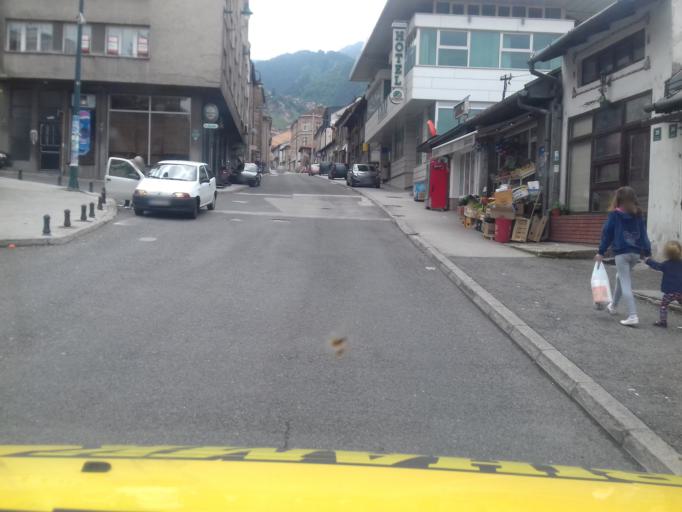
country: BA
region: Federation of Bosnia and Herzegovina
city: Kobilja Glava
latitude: 43.8553
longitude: 18.4300
